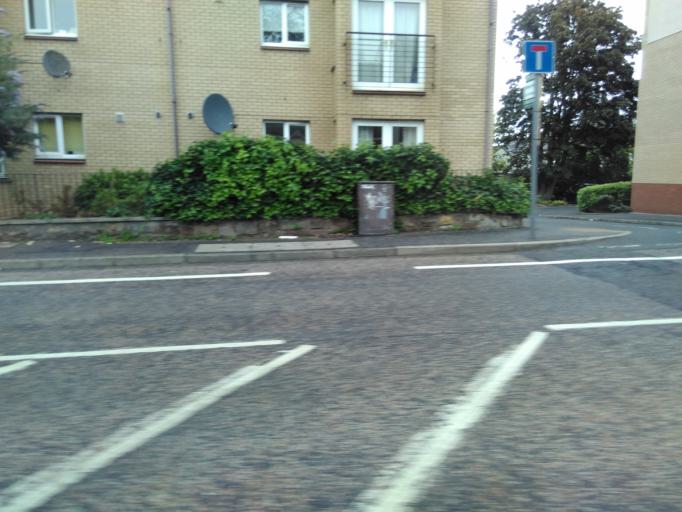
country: GB
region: Scotland
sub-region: Midlothian
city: Loanhead
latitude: 55.9197
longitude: -3.1576
